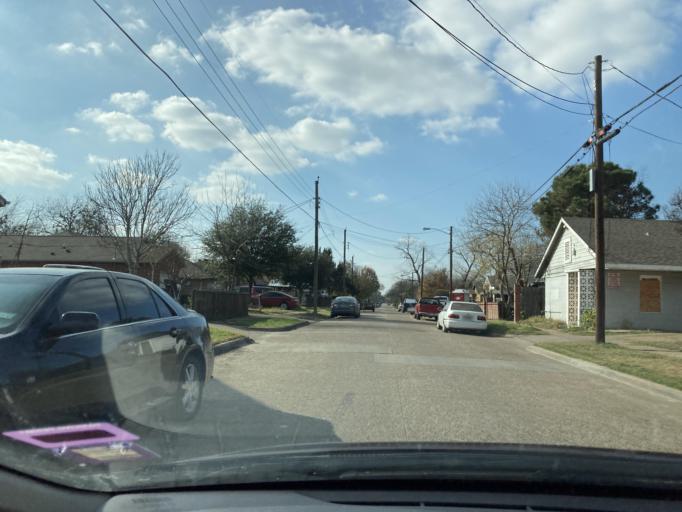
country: US
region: Texas
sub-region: Dallas County
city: Dallas
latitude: 32.7810
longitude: -96.8485
